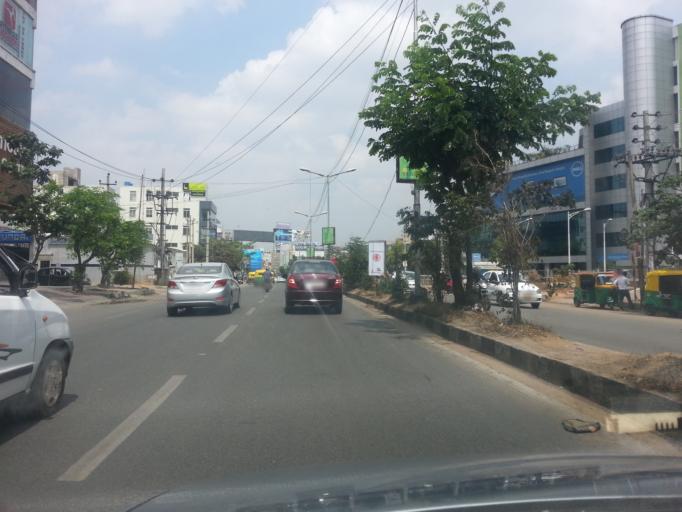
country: IN
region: Karnataka
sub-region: Bangalore Urban
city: Bangalore
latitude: 12.9523
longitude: 77.6401
